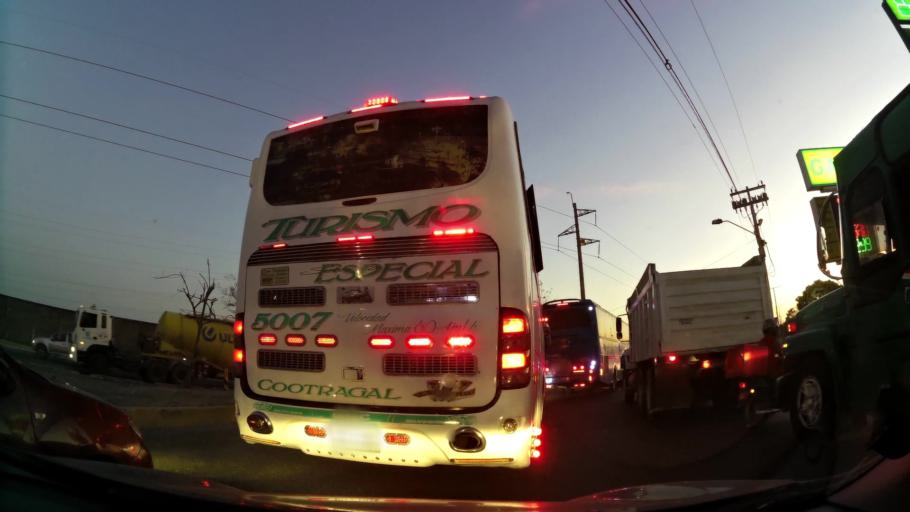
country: CO
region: Atlantico
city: Soledad
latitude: 10.9311
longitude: -74.7838
